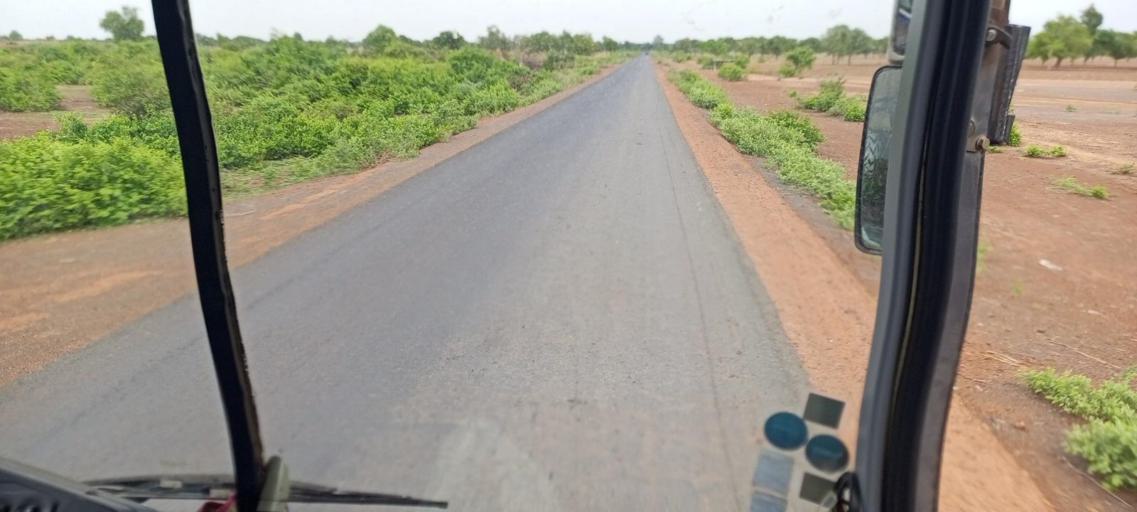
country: ML
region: Segou
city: Bla
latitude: 12.7489
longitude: -5.7325
